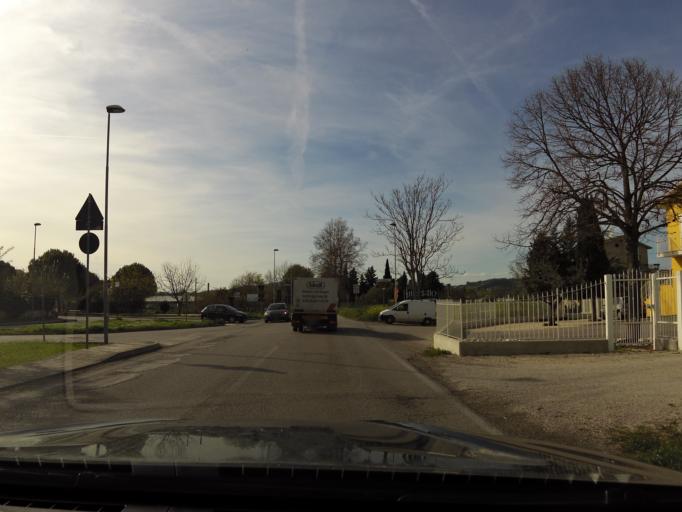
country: IT
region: The Marches
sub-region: Provincia di Ancona
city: Villa Musone
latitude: 43.4478
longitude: 13.6062
